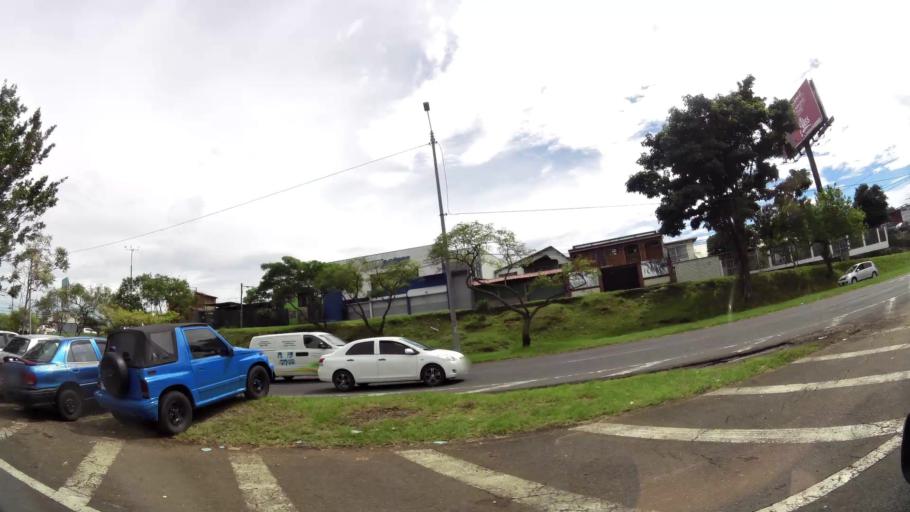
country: CR
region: San Jose
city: San Pedro
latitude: 9.9242
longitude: -84.0571
